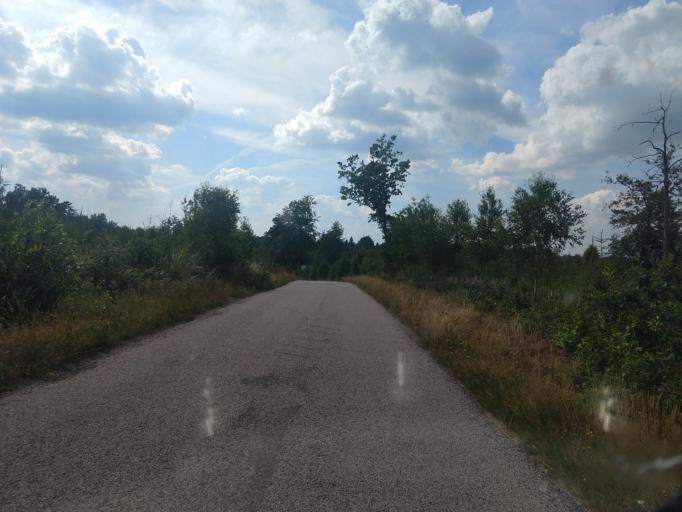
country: SE
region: Blekinge
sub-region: Karlskrona Kommun
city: Rodeby
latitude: 56.2450
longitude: 15.5536
